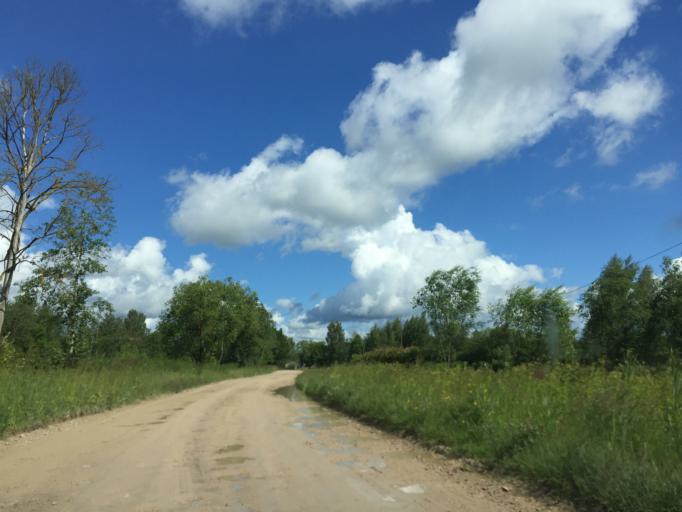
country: LV
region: Lecava
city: Iecava
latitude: 56.6165
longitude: 24.1884
